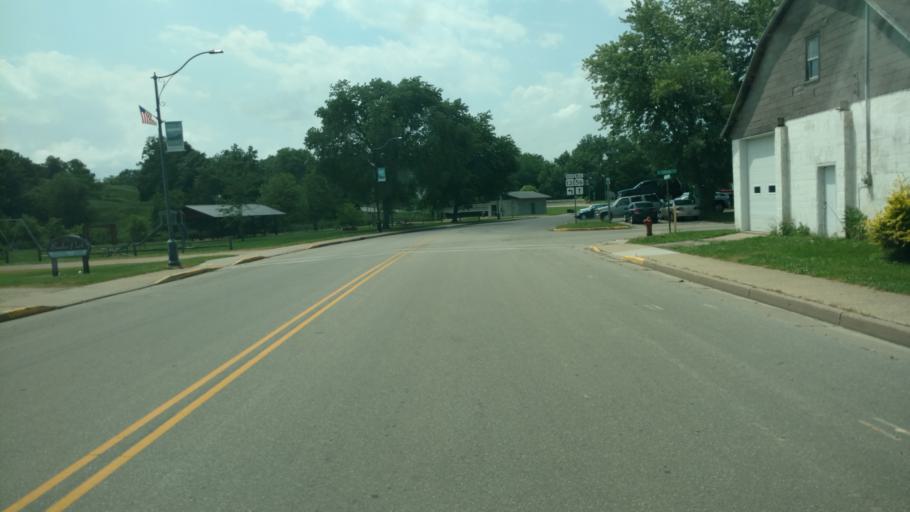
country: US
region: Wisconsin
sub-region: Vernon County
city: Viroqua
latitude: 43.5061
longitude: -90.6716
